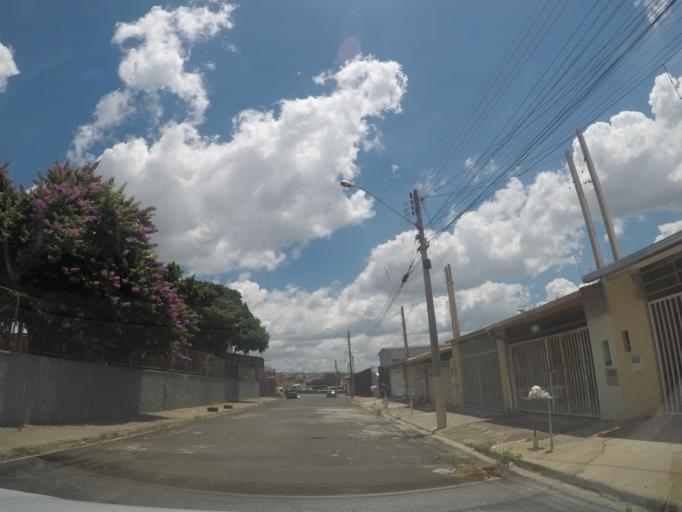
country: BR
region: Sao Paulo
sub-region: Hortolandia
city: Hortolandia
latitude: -22.8196
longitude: -47.2014
